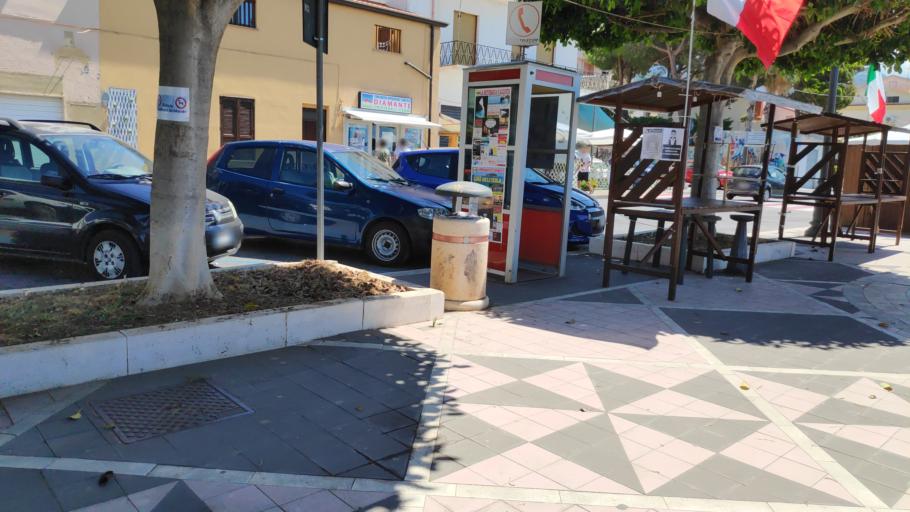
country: IT
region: Calabria
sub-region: Provincia di Cosenza
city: Diamante
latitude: 39.6759
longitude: 15.8205
